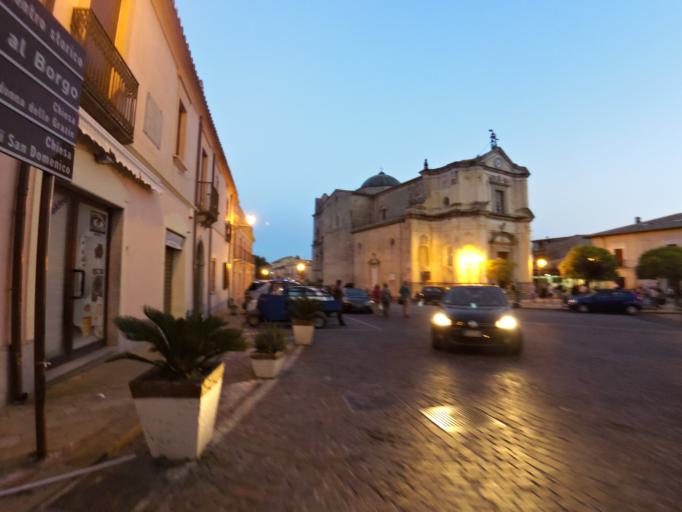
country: IT
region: Calabria
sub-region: Provincia di Reggio Calabria
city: Stilo
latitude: 38.4776
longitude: 16.4688
